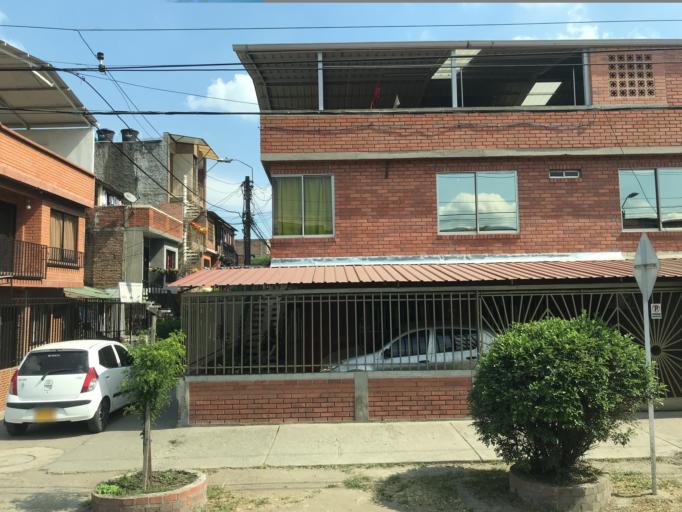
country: CO
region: Valle del Cauca
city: Cali
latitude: 3.4898
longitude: -76.4977
